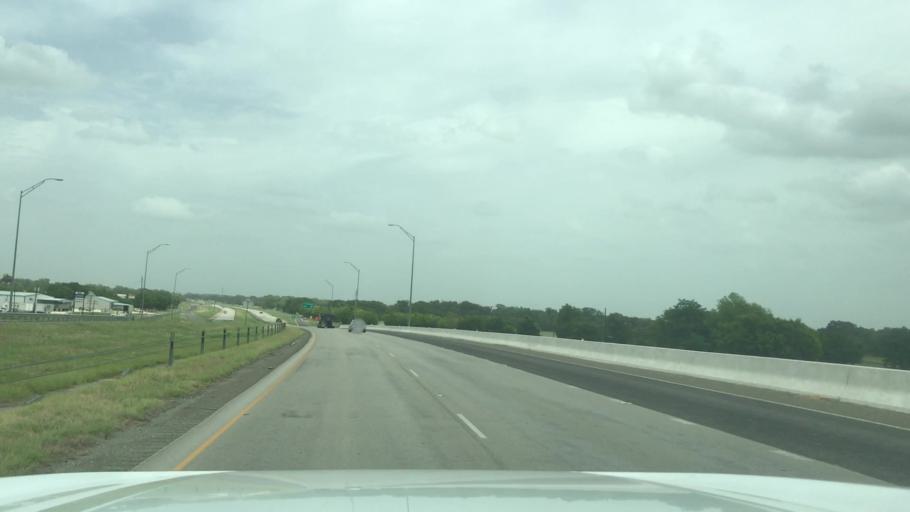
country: US
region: Texas
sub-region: McLennan County
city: Beverly
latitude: 31.5197
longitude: -97.0884
